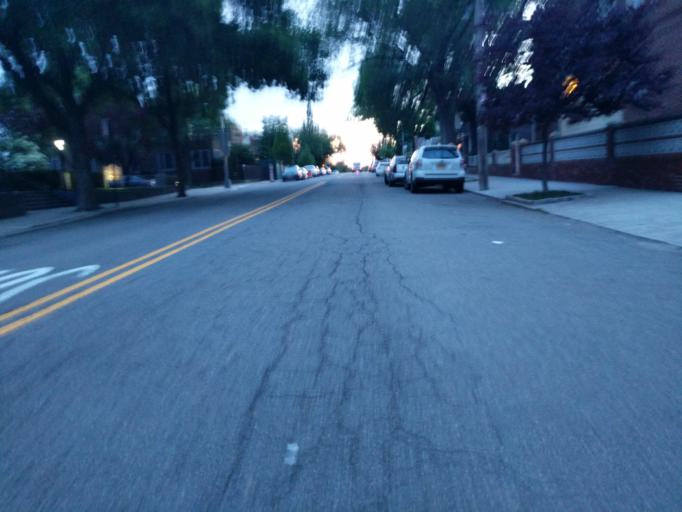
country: US
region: New York
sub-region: Queens County
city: Long Island City
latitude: 40.7725
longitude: -73.9005
